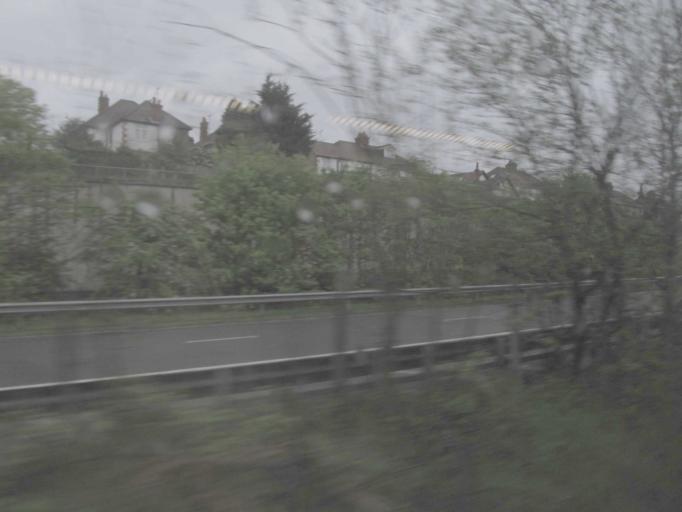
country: GB
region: England
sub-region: Wokingham
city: Earley
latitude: 51.4464
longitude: -0.9296
